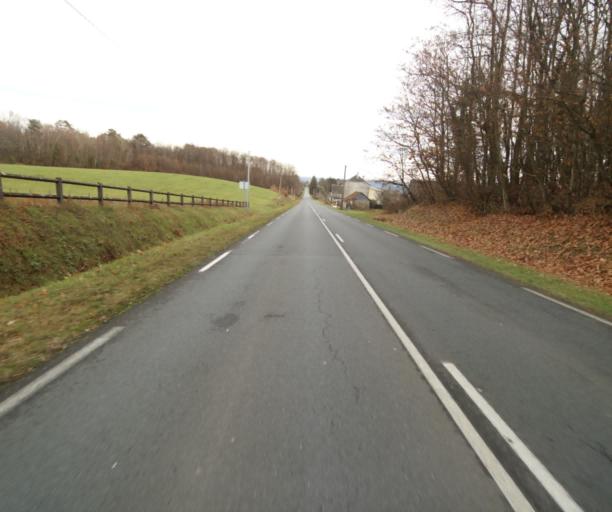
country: FR
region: Limousin
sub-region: Departement de la Correze
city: Chameyrat
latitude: 45.2691
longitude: 1.6965
